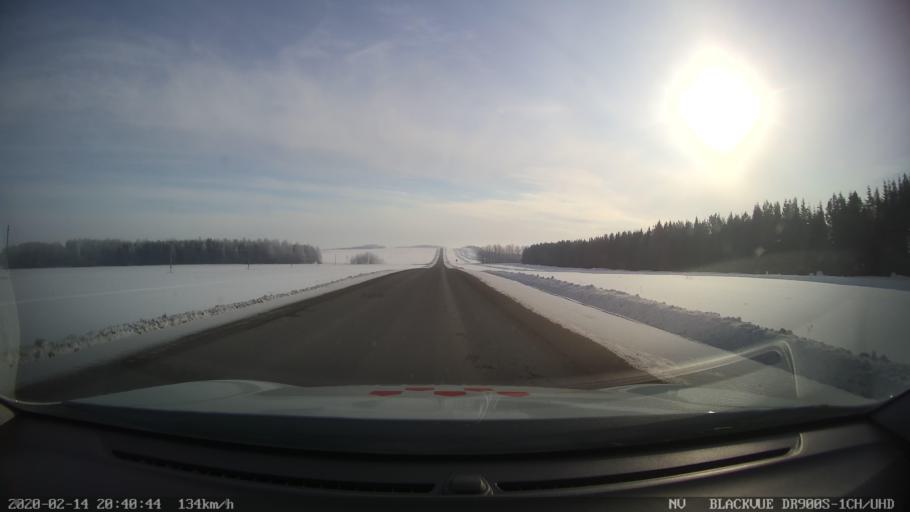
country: RU
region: Tatarstan
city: Kuybyshevskiy Zaton
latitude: 55.3373
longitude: 49.0988
